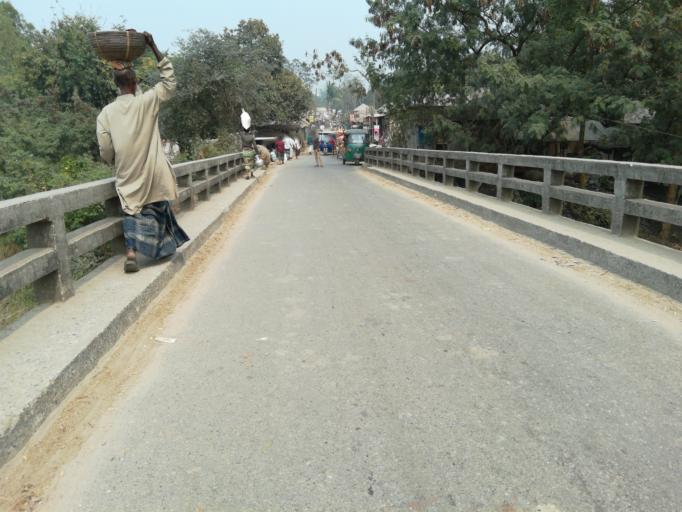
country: BD
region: Dhaka
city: Nagarpur
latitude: 23.9016
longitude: 89.8746
